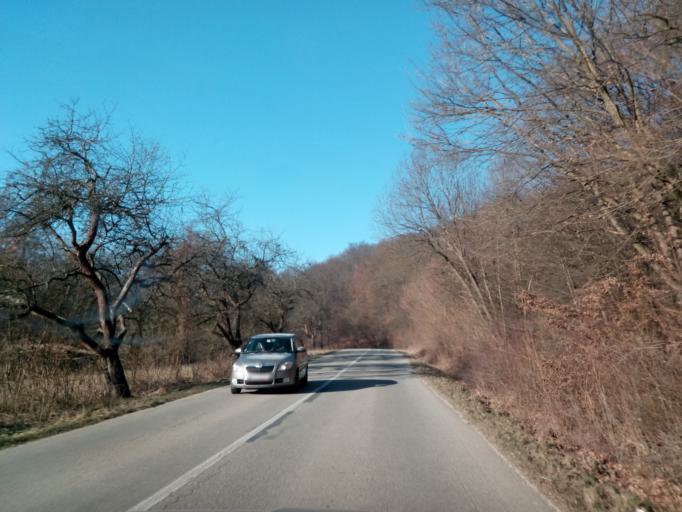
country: SK
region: Kosicky
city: Medzev
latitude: 48.6921
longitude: 20.9541
